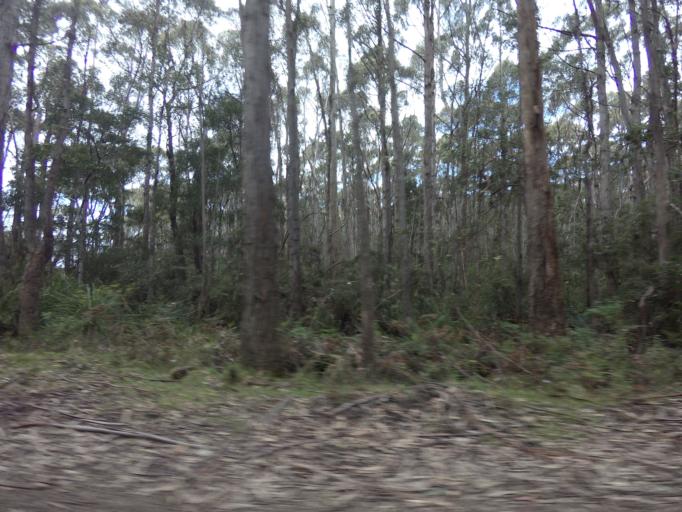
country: AU
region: Tasmania
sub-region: Huon Valley
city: Geeveston
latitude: -43.4224
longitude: 147.0108
